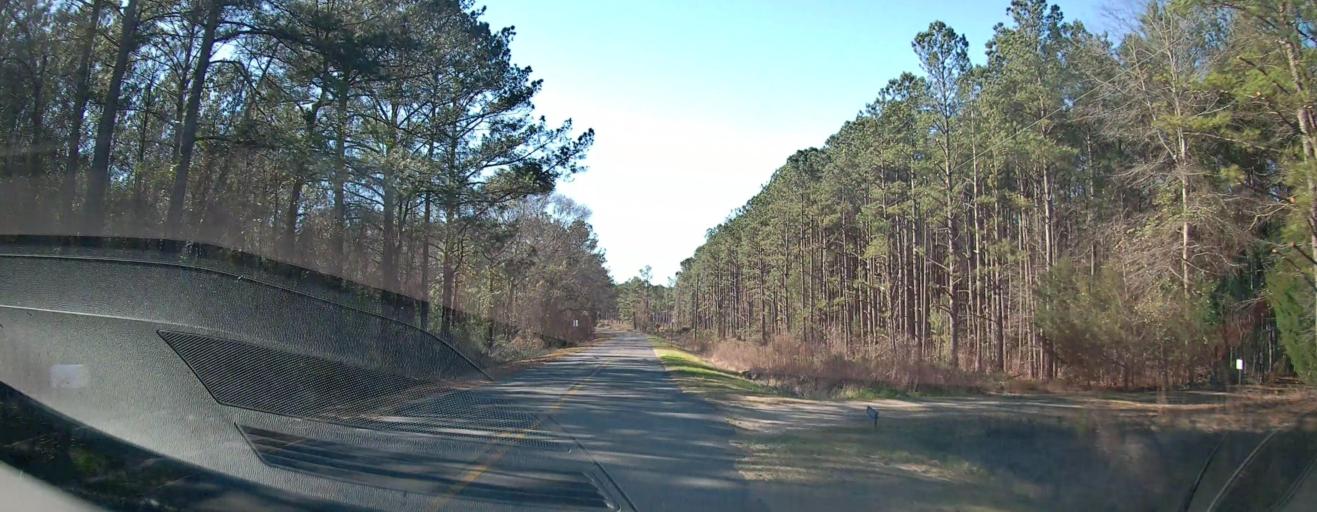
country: US
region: Georgia
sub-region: Taylor County
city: Butler
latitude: 32.6360
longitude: -84.2843
